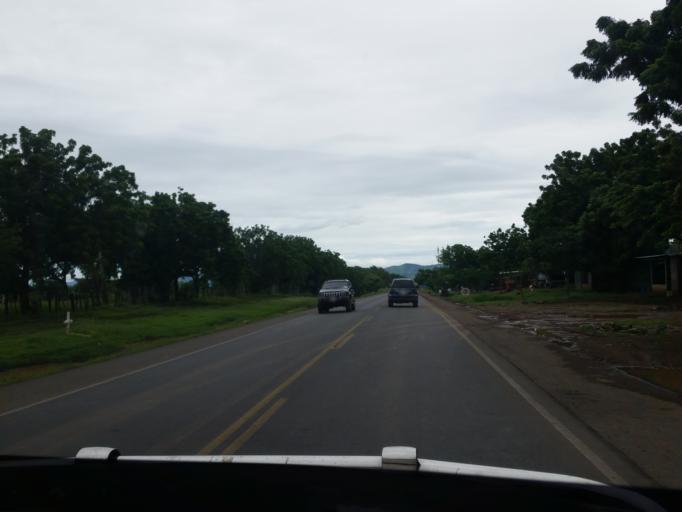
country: NI
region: Managua
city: Tipitapa
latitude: 12.2685
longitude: -86.0751
